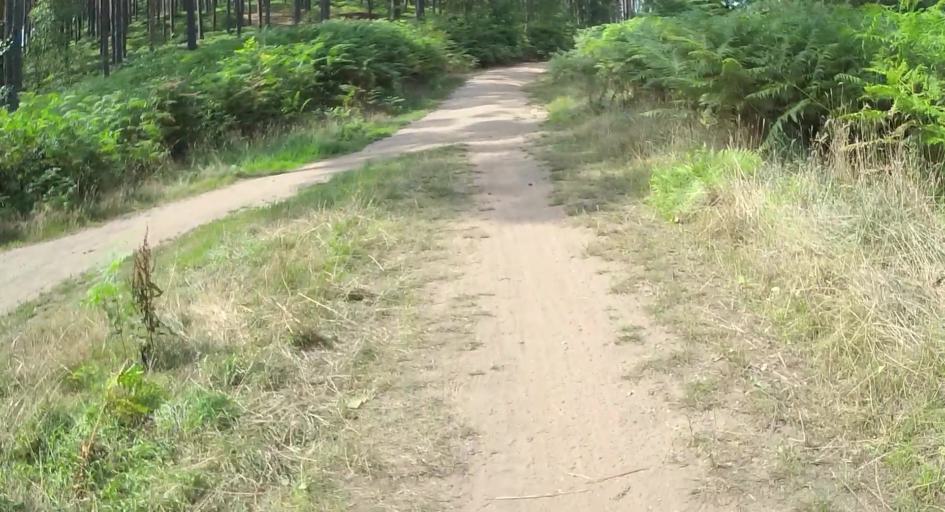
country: GB
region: England
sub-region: Surrey
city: Farnham
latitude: 51.1928
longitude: -0.7721
